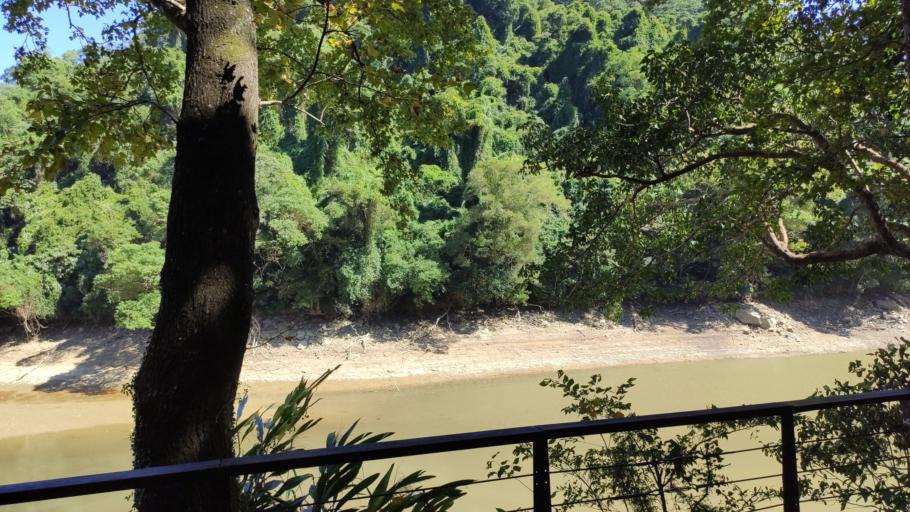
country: TW
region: Taiwan
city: Daxi
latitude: 24.8437
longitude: 121.3022
